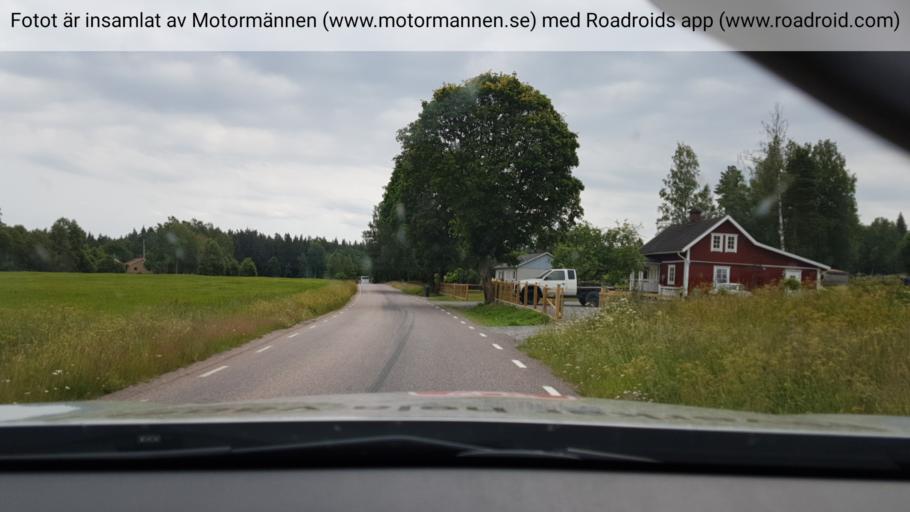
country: SE
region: Vaestra Goetaland
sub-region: Tidaholms Kommun
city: Tidaholm
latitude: 58.0719
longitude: 13.9248
